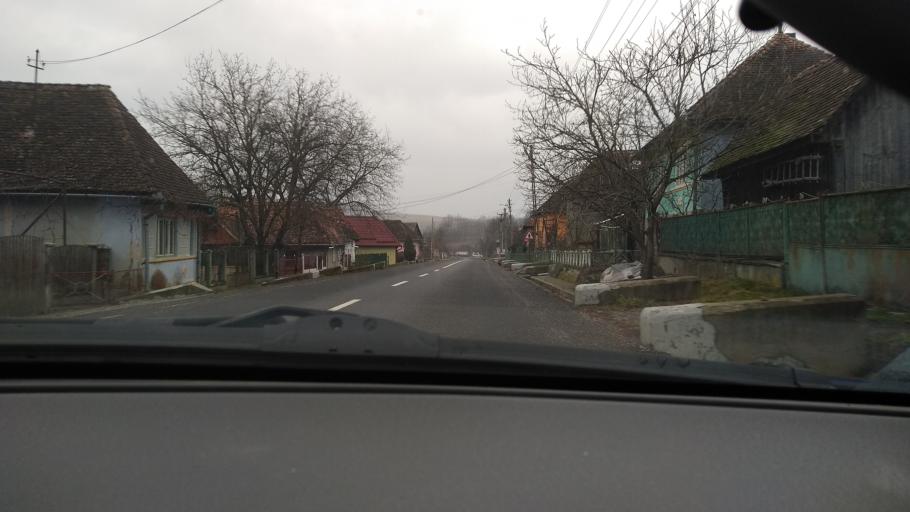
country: RO
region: Mures
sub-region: Comuna Magherani
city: Magherani
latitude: 46.5681
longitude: 24.9210
